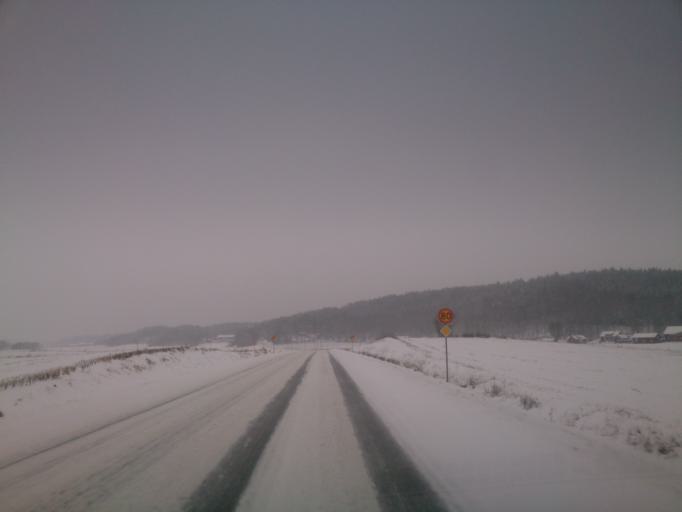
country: SE
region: OEstergoetland
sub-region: Norrkopings Kommun
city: Skarblacka
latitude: 58.6007
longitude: 15.8307
